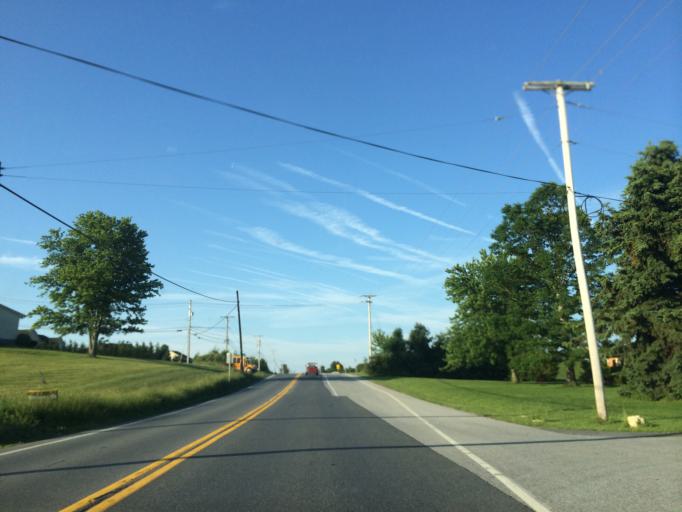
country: US
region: Maryland
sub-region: Carroll County
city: Sykesville
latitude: 39.3905
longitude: -77.0184
